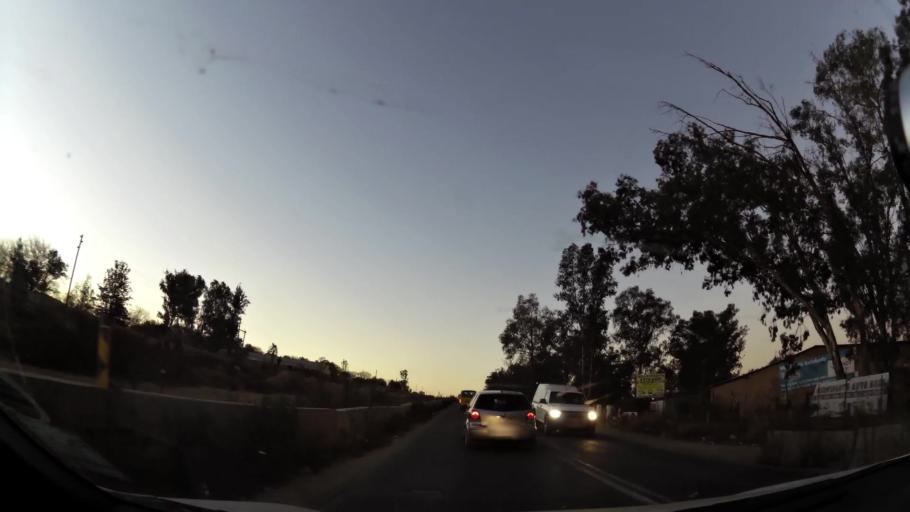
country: ZA
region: Gauteng
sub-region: City of Johannesburg Metropolitan Municipality
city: Diepsloot
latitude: -25.9497
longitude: 28.0186
